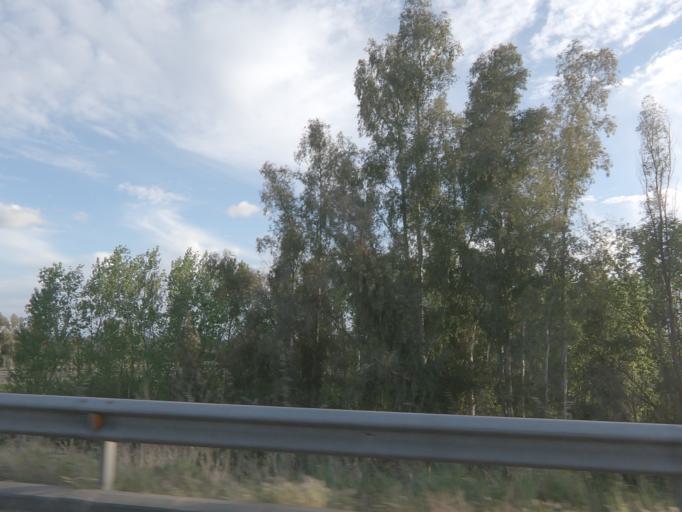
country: ES
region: Extremadura
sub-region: Provincia de Badajoz
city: Badajoz
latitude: 38.9190
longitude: -6.9556
